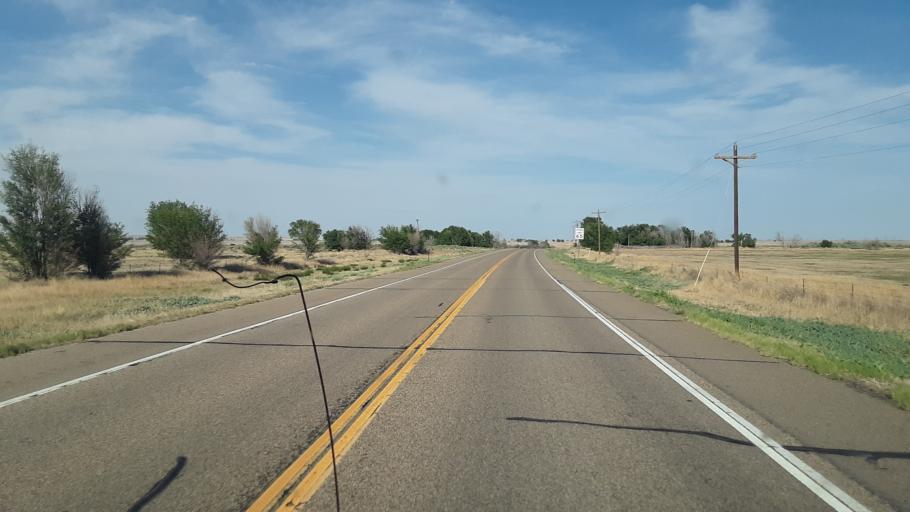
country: US
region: Colorado
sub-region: Bent County
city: Las Animas
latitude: 38.1129
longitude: -103.0917
